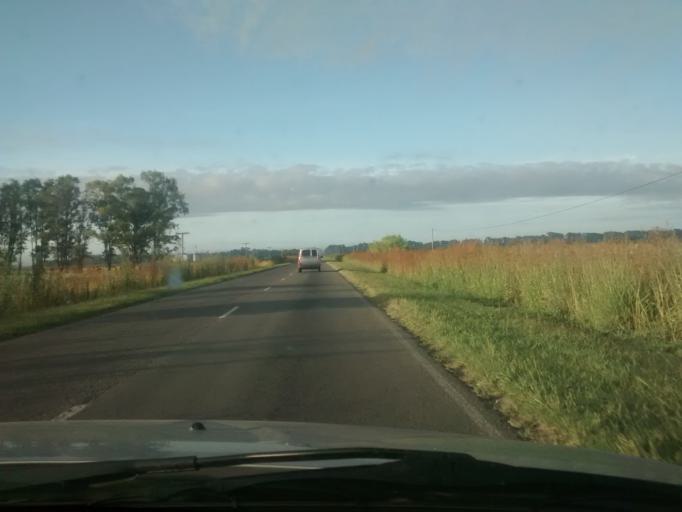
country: AR
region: Buenos Aires
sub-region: Partido de Brandsen
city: Brandsen
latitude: -35.1182
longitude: -58.1851
